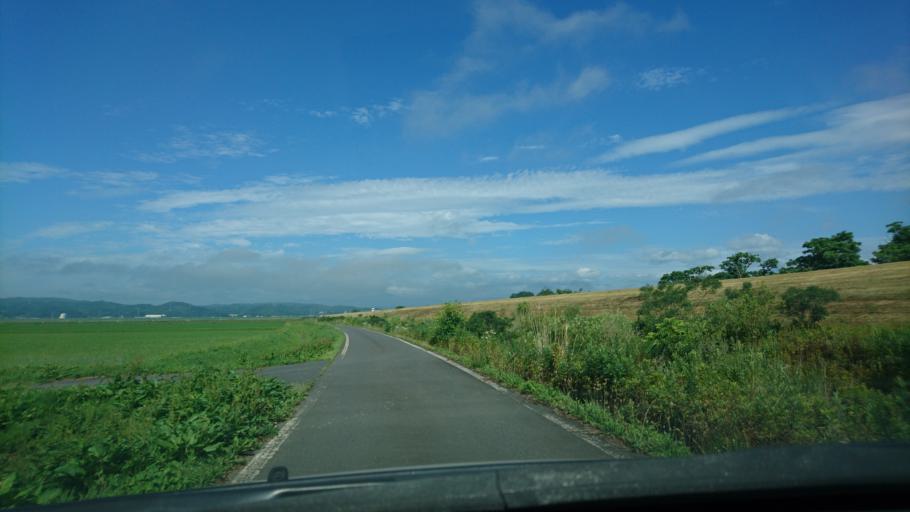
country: JP
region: Iwate
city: Ichinoseki
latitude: 38.9743
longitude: 141.1498
